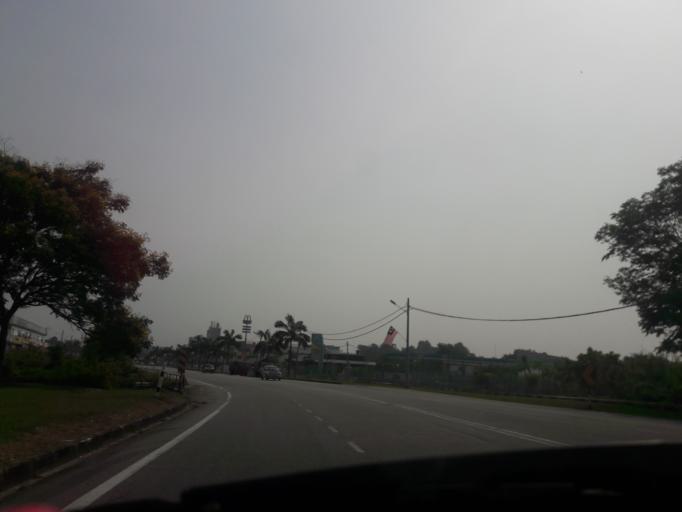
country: MY
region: Kedah
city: Kulim
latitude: 5.3816
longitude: 100.5449
